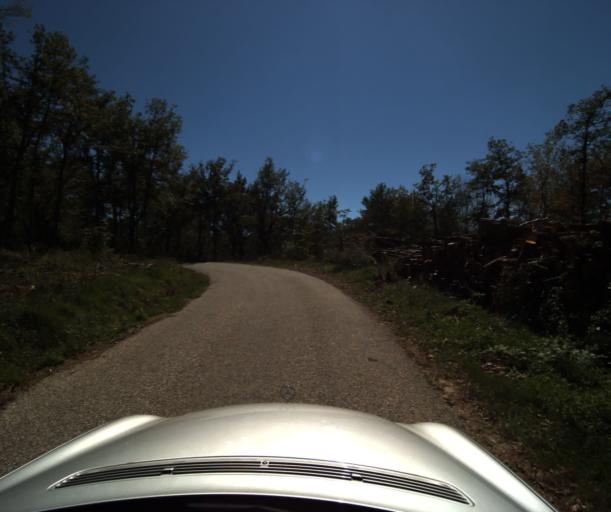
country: FR
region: Midi-Pyrenees
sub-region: Departement de l'Ariege
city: Lavelanet
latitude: 42.9695
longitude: 1.9041
